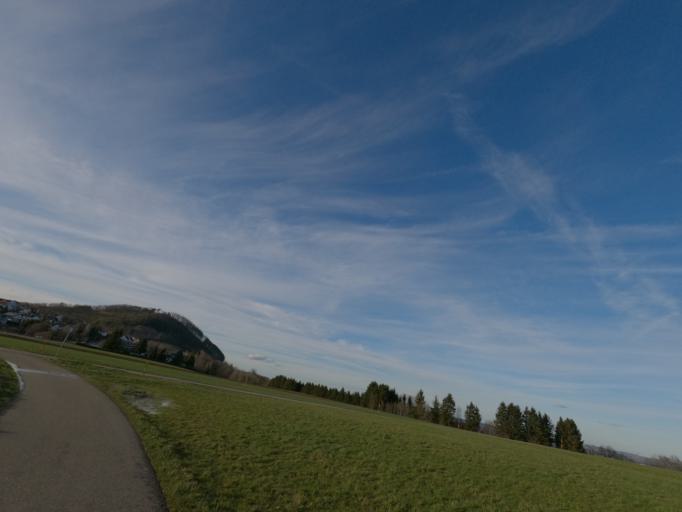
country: DE
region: Baden-Wuerttemberg
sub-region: Regierungsbezirk Stuttgart
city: Waldstetten
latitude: 48.7468
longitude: 9.8011
